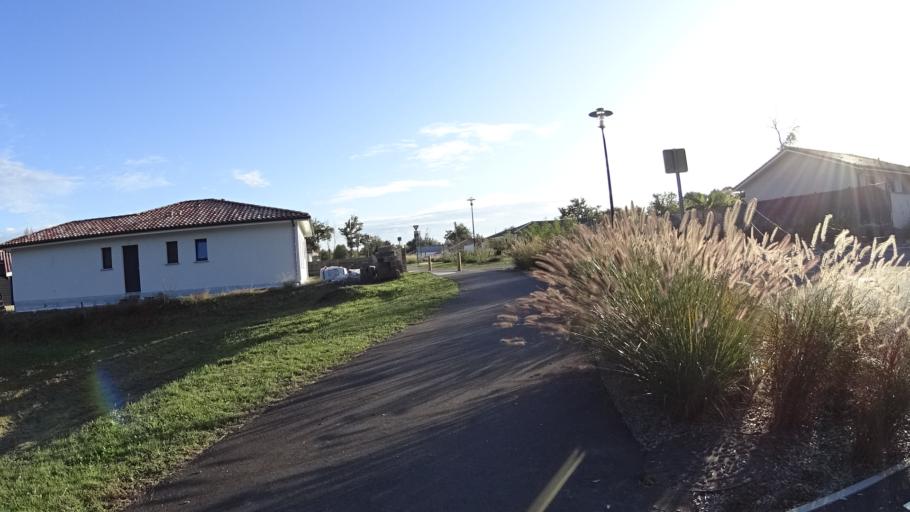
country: FR
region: Aquitaine
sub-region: Departement des Landes
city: Saint-Paul-les-Dax
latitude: 43.7417
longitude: -1.0459
